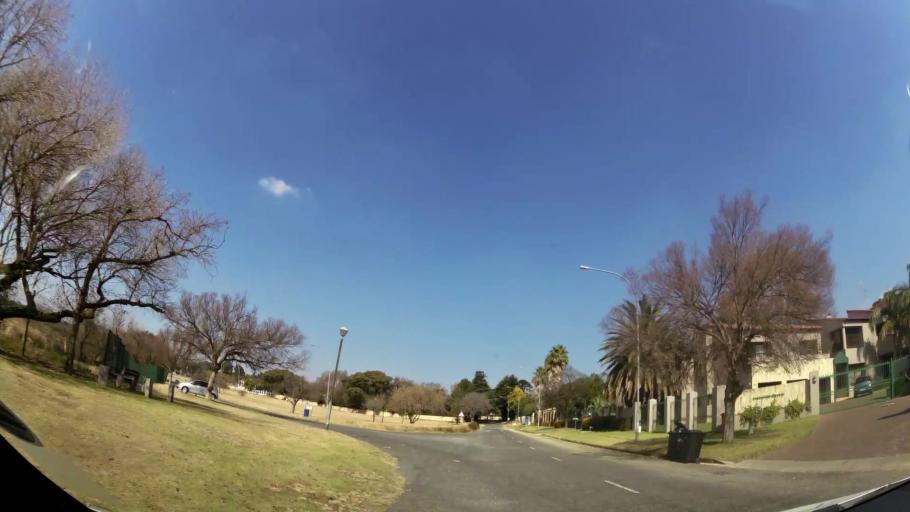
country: ZA
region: Gauteng
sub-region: Ekurhuleni Metropolitan Municipality
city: Benoni
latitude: -26.1950
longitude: 28.2908
